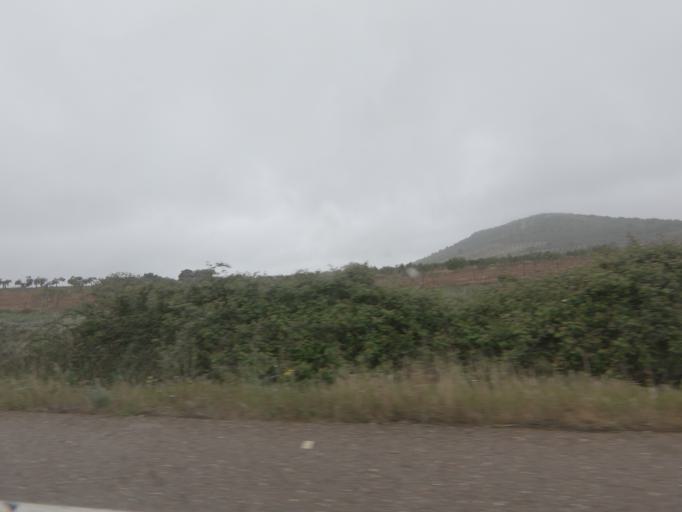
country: ES
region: Extremadura
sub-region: Provincia de Badajoz
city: Puebla de Obando
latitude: 39.1826
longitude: -6.6080
